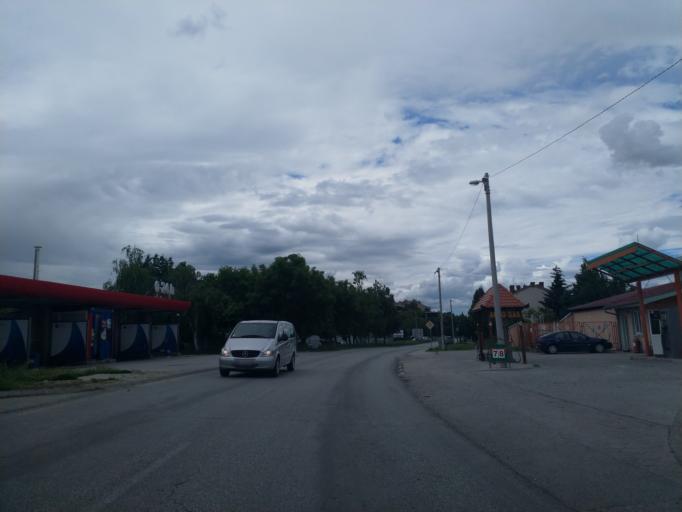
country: RS
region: Central Serbia
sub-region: Pomoravski Okrug
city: Jagodina
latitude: 43.9655
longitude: 21.2777
